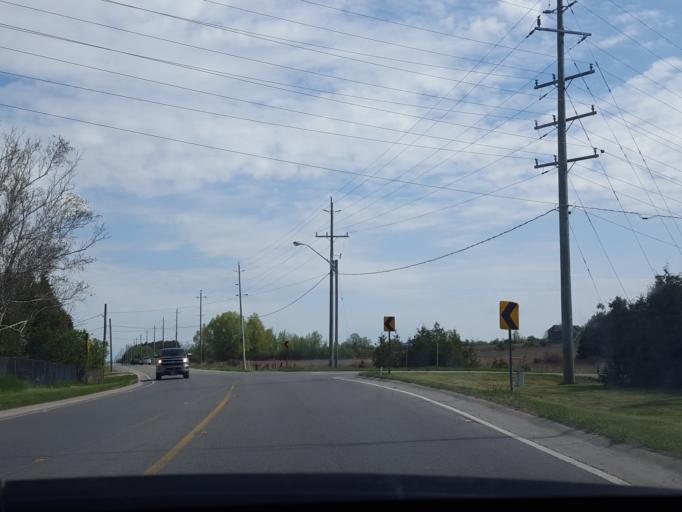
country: CA
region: Ontario
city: Uxbridge
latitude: 44.1554
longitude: -78.8995
